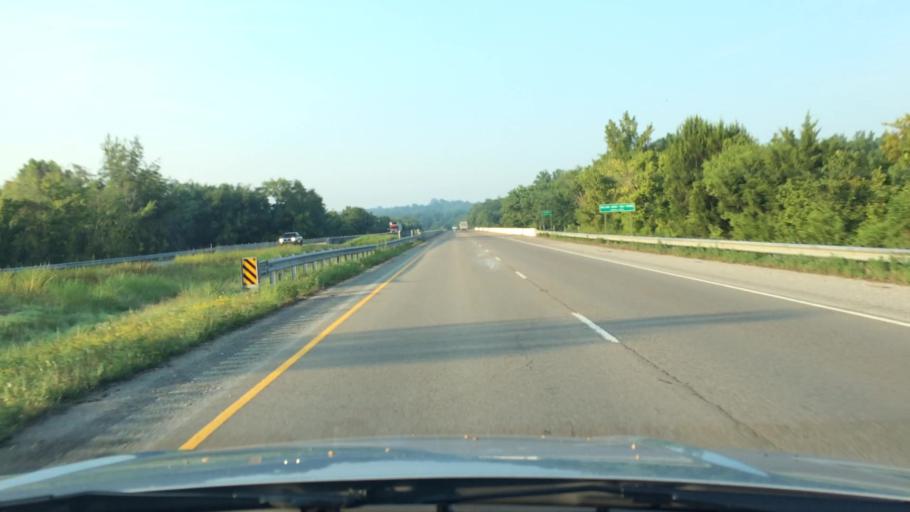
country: US
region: Tennessee
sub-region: Giles County
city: Pulaski
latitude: 35.1973
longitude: -87.0638
